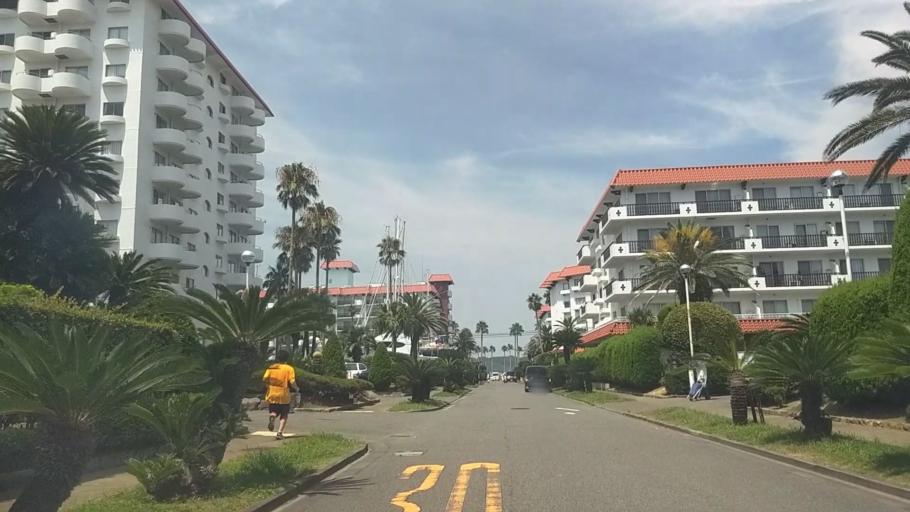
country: JP
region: Kanagawa
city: Kamakura
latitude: 35.2971
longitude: 139.5536
